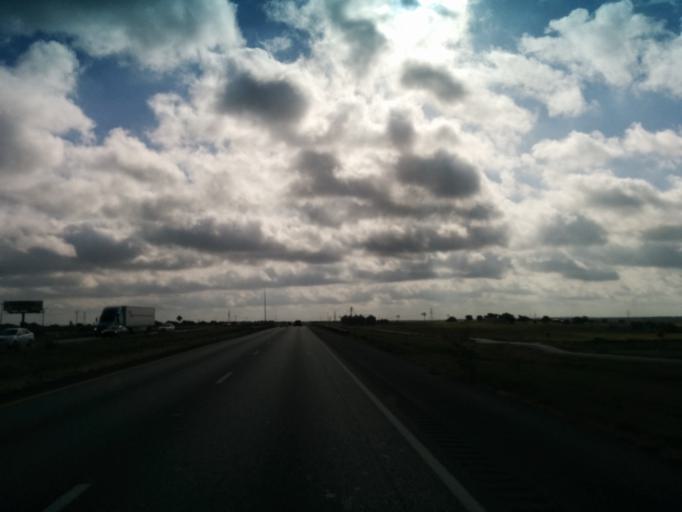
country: US
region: Texas
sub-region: Guadalupe County
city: McQueeney
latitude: 29.5397
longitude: -98.0743
